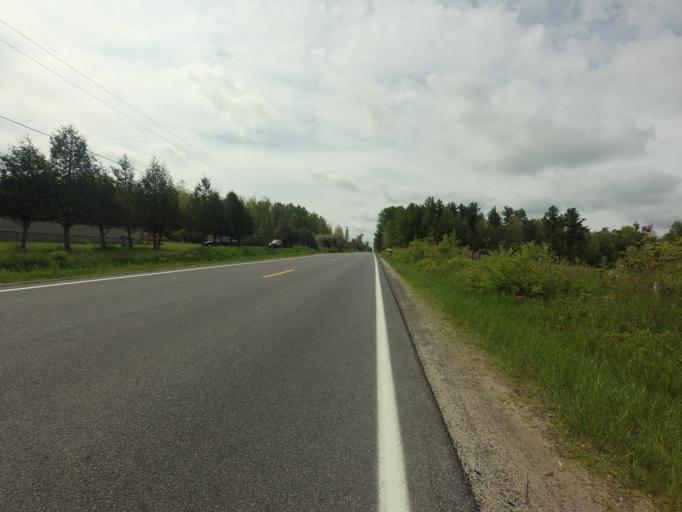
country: CA
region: Ontario
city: Cornwall
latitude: 44.7412
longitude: -74.6664
